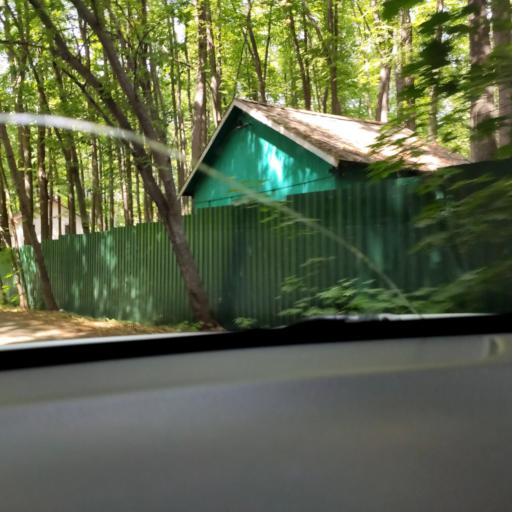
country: RU
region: Tatarstan
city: Verkhniy Uslon
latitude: 55.6546
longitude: 49.0285
